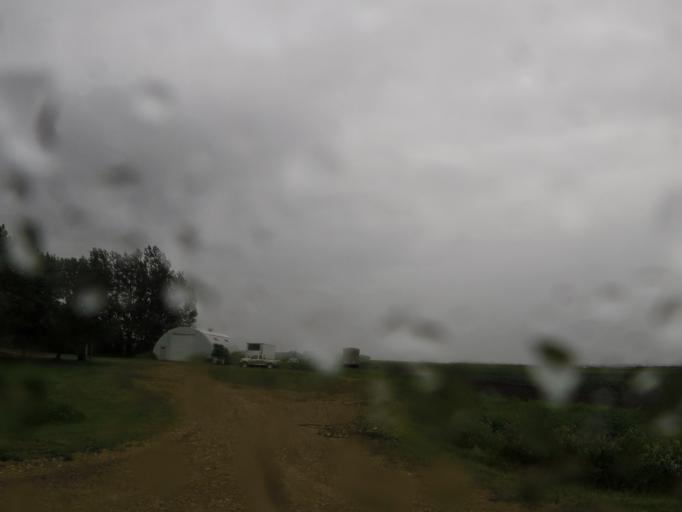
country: US
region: North Dakota
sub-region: Walsh County
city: Grafton
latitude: 48.4568
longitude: -97.4046
